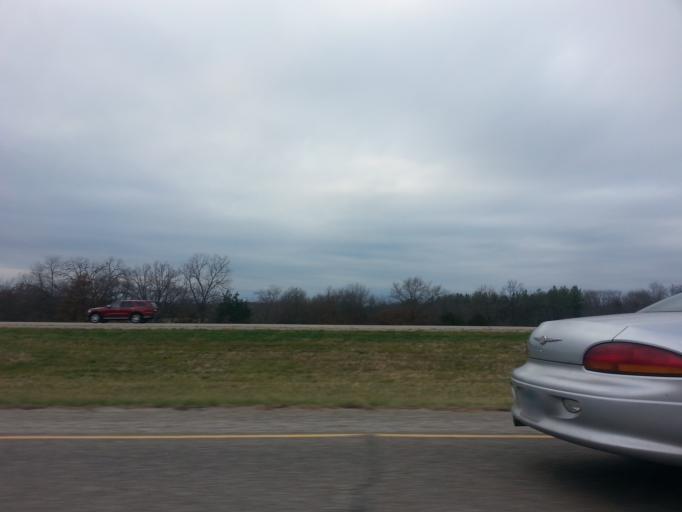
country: US
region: Iowa
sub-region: Henry County
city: Mount Pleasant
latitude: 40.9043
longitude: -91.5508
